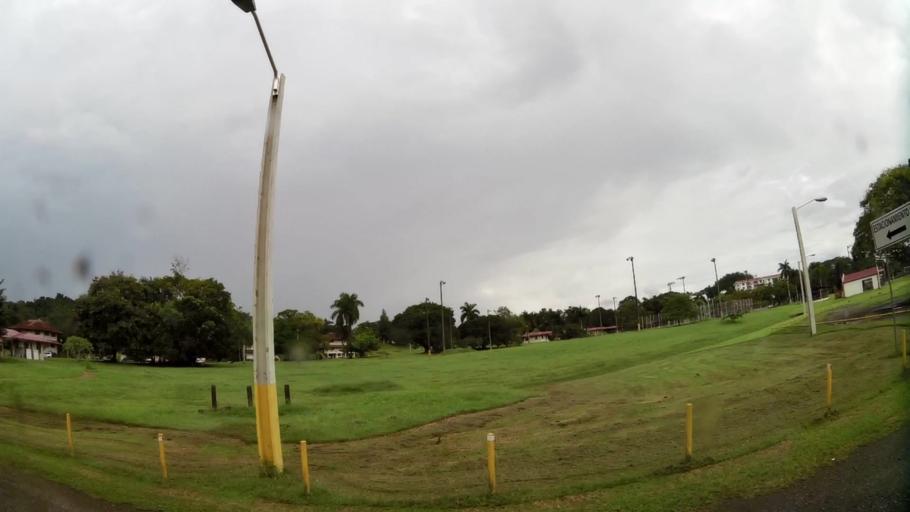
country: PA
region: Panama
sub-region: Distrito de Panama
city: Ancon
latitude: 9.0024
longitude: -79.5809
